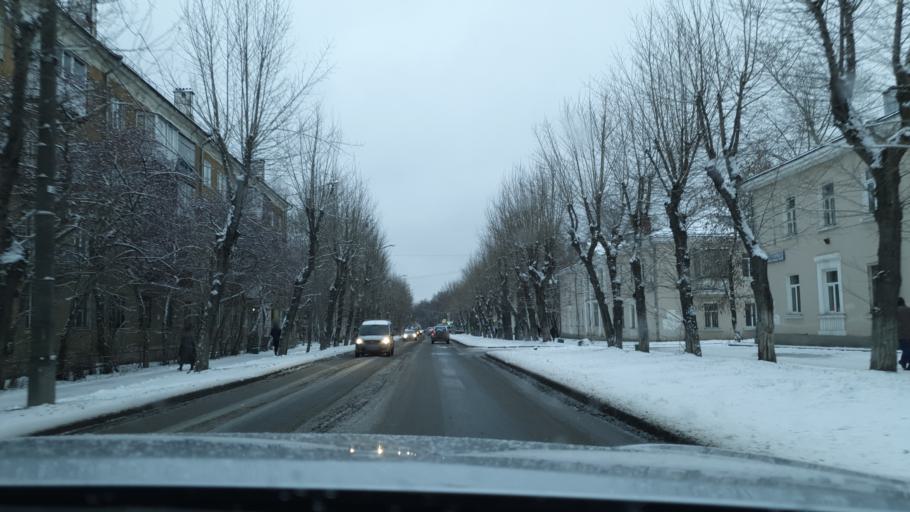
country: RU
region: Sverdlovsk
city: Istok
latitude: 56.7549
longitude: 60.7083
